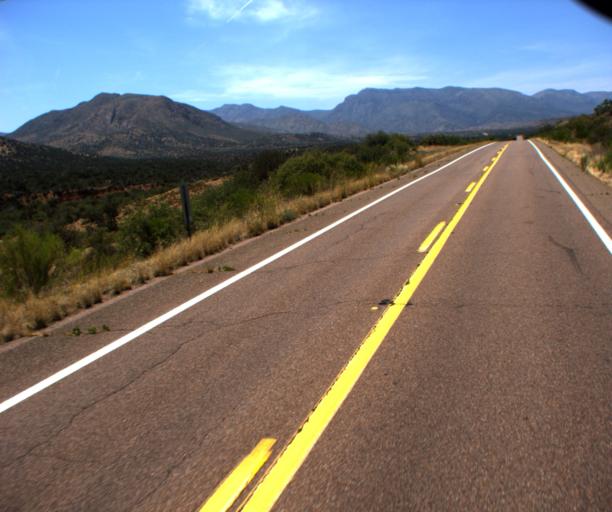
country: US
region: Arizona
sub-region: Gila County
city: Tonto Basin
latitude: 34.0160
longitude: -111.3284
